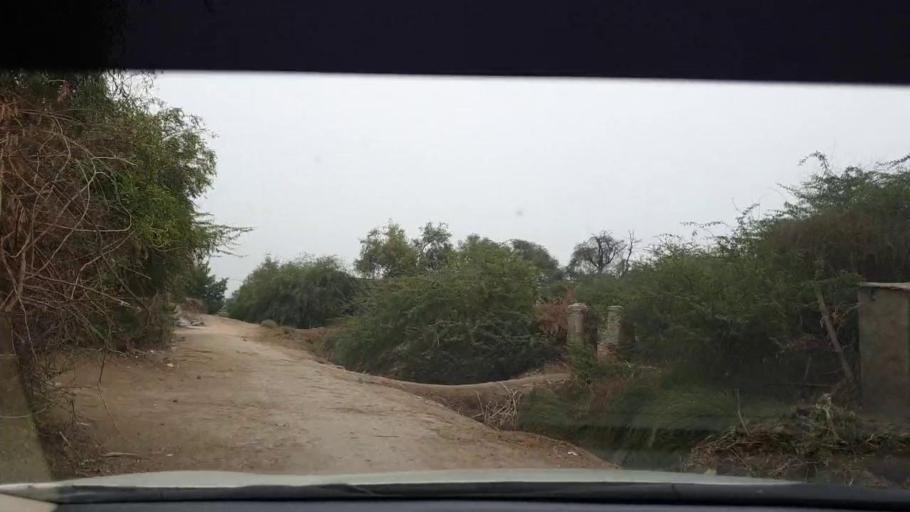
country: PK
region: Sindh
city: Berani
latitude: 25.8752
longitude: 68.7946
